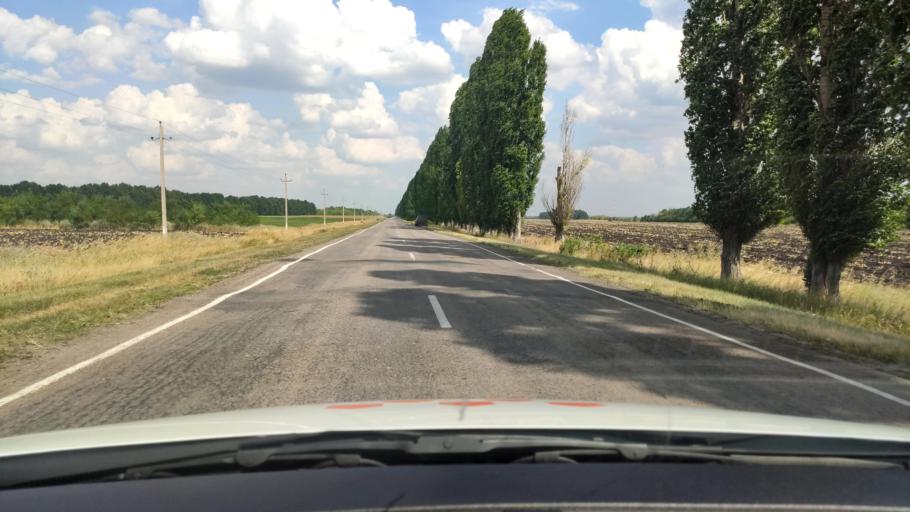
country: RU
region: Voronezj
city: Sadovoye
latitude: 51.7597
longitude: 40.4415
